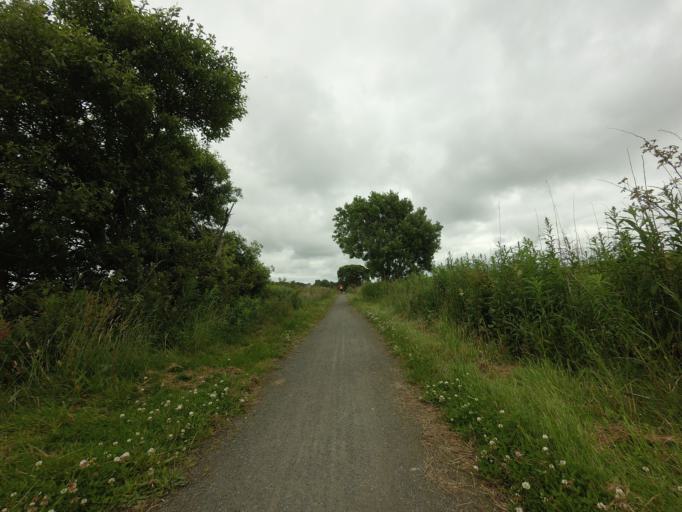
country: GB
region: Scotland
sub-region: Aberdeenshire
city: Ellon
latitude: 57.4700
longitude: -2.1209
